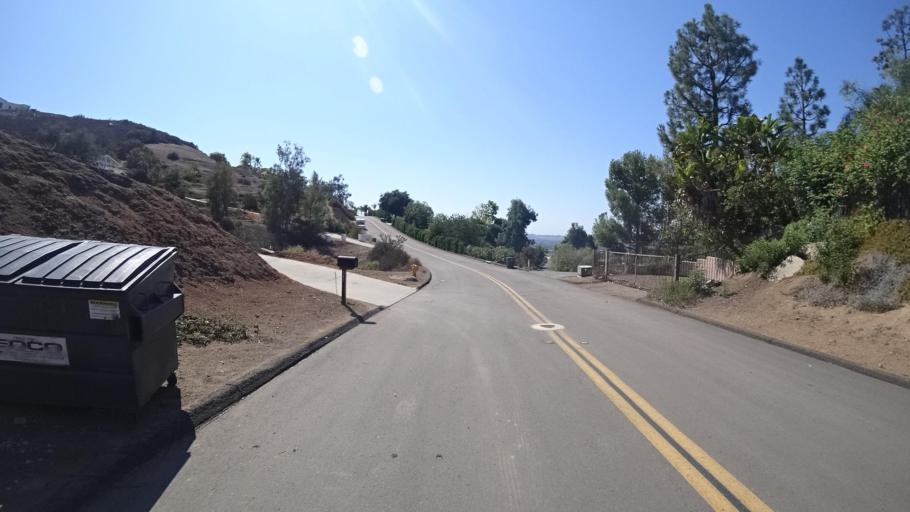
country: US
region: California
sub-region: San Diego County
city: Granite Hills
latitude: 32.7997
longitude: -116.8950
